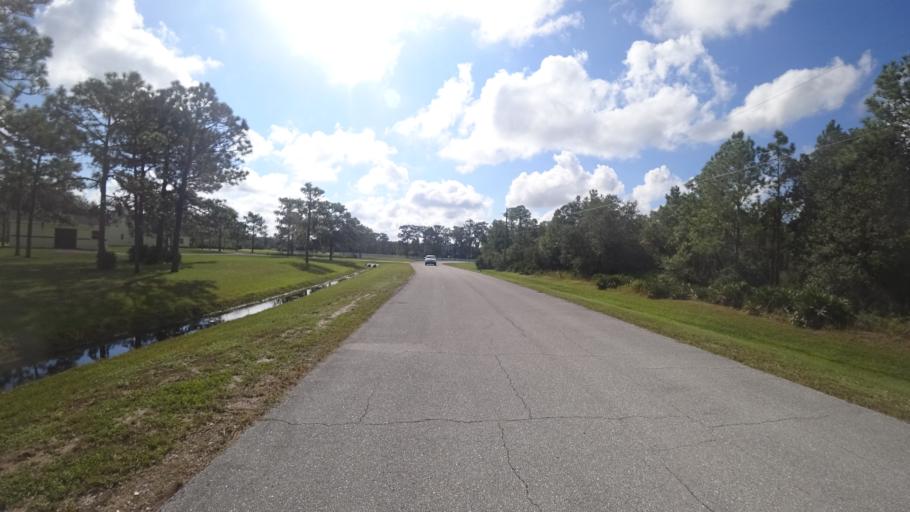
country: US
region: Florida
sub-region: Sarasota County
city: The Meadows
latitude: 27.3997
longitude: -82.3400
